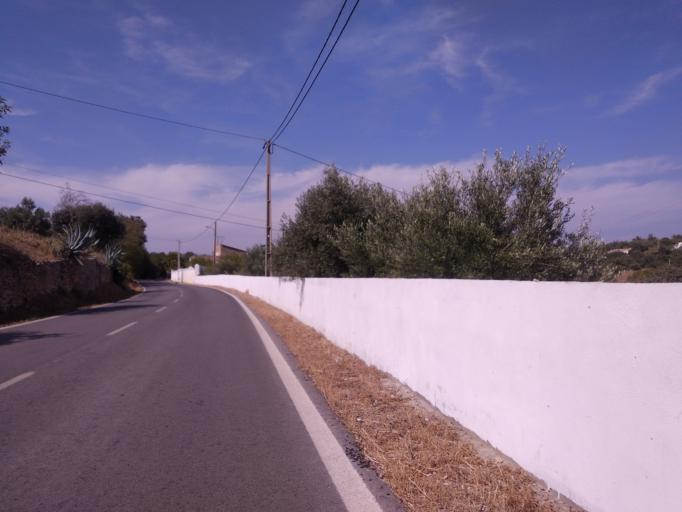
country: PT
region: Faro
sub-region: Faro
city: Santa Barbara de Nexe
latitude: 37.1152
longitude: -7.9595
